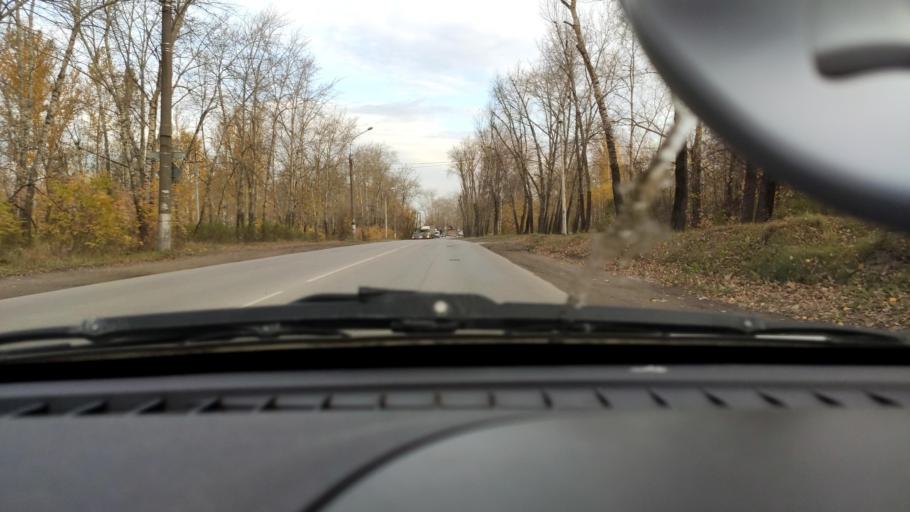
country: RU
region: Perm
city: Perm
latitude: 58.1190
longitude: 56.3687
